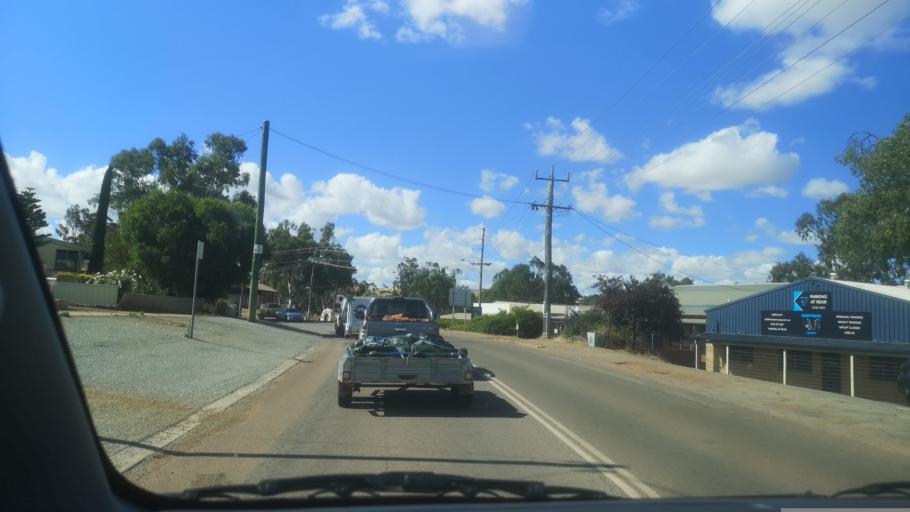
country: AU
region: Western Australia
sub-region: Toodyay
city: Toodyay
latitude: -31.5569
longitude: 116.4761
